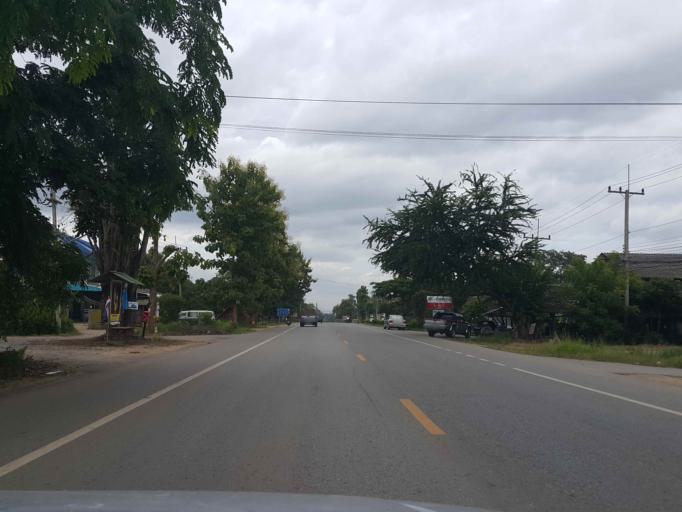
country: TH
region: Lamphun
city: Li
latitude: 17.7772
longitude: 98.9558
